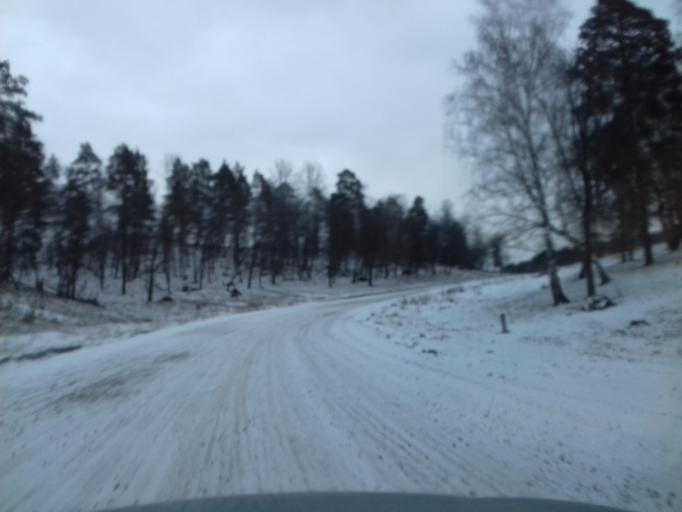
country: RU
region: Bashkortostan
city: Starosubkhangulovo
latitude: 53.0896
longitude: 57.4367
